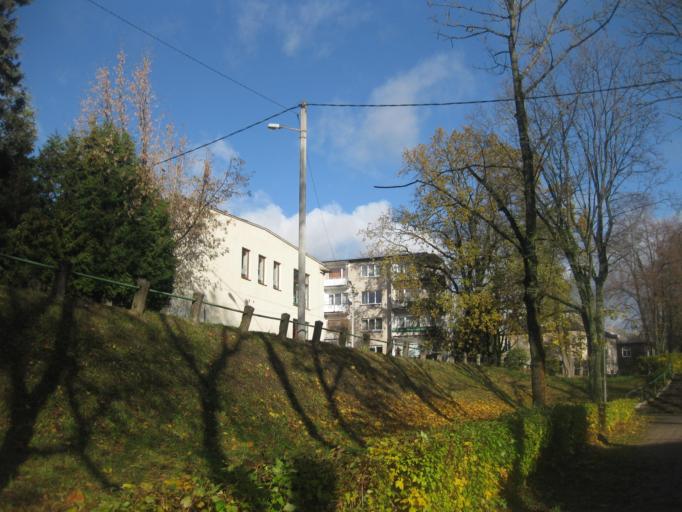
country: LT
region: Kauno apskritis
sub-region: Kaunas
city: Kaunas
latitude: 54.9008
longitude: 23.9254
